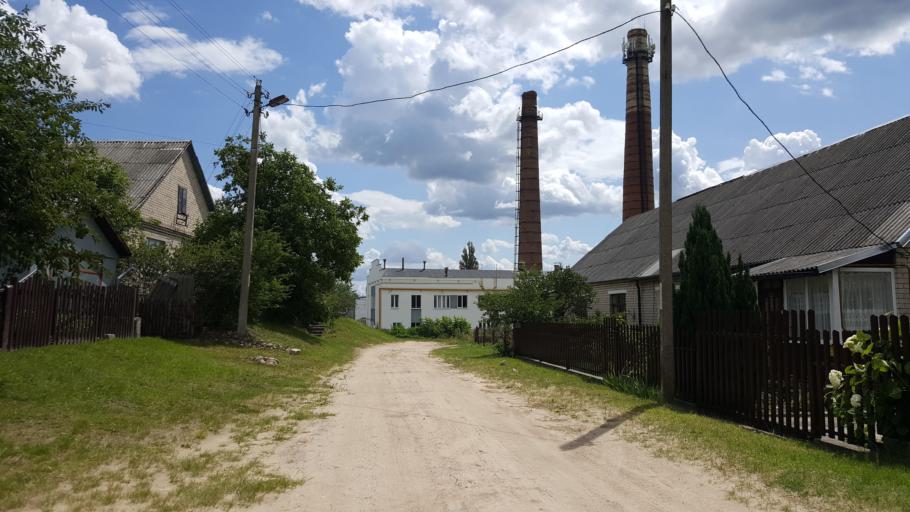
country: BY
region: Brest
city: Kamyanyets
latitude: 52.4002
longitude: 23.8294
